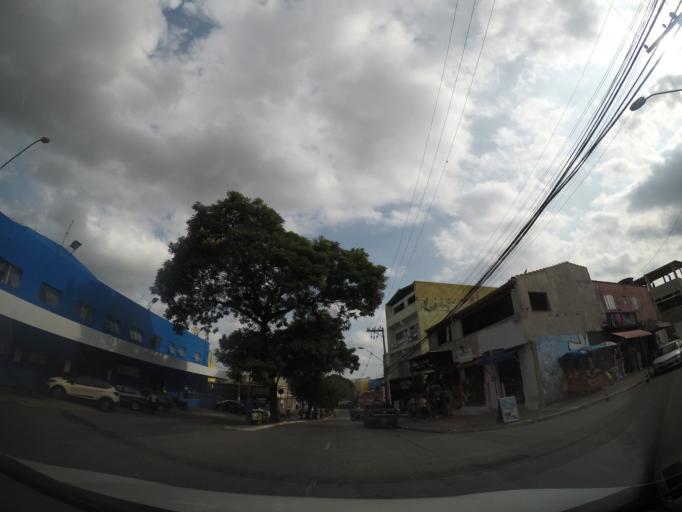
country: BR
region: Sao Paulo
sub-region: Guarulhos
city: Guarulhos
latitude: -23.4101
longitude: -46.4541
